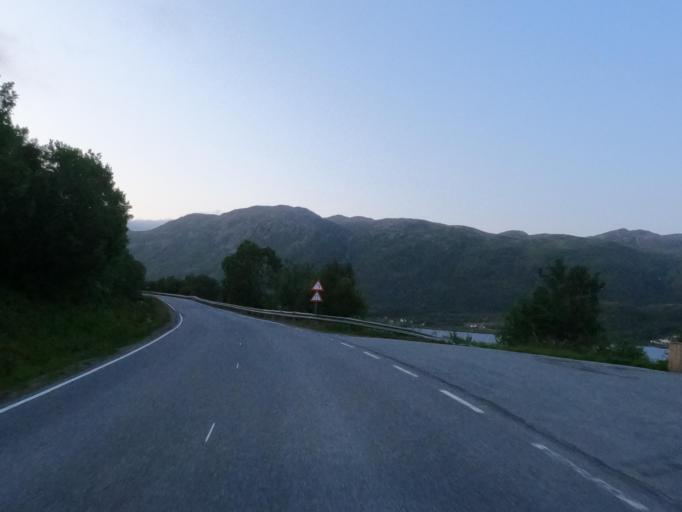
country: NO
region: Nordland
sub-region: Lodingen
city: Lodingen
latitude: 68.5640
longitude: 15.7988
